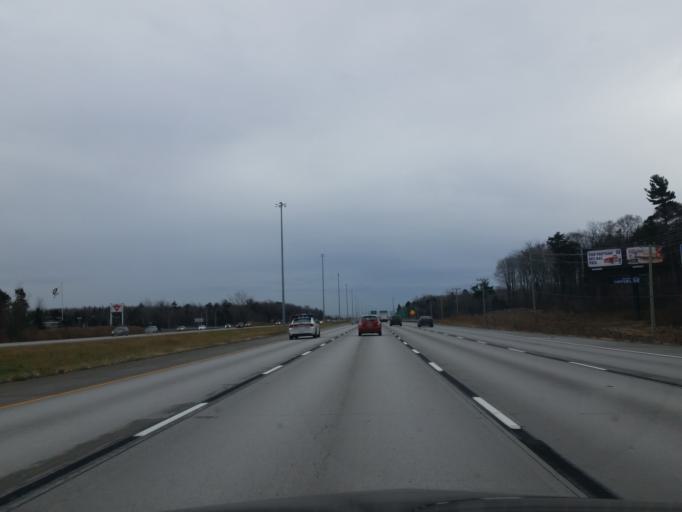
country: CA
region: Quebec
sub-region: Laurentides
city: Blainville
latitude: 45.6611
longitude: -73.8907
